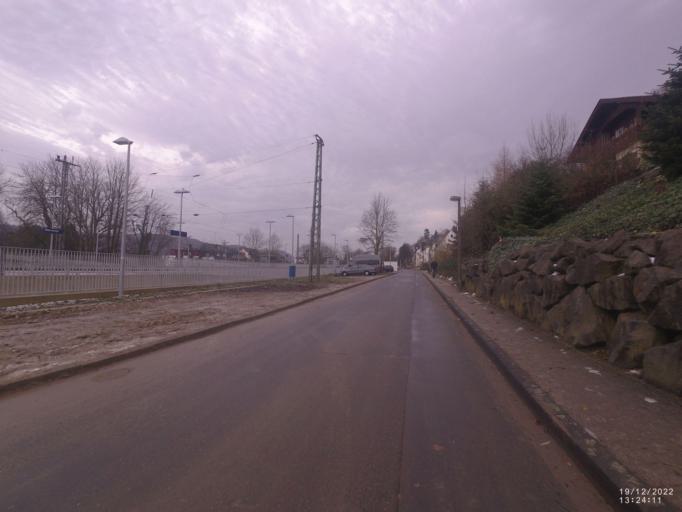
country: DE
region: Rheinland-Pfalz
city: Unkel
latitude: 50.6115
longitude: 7.2074
